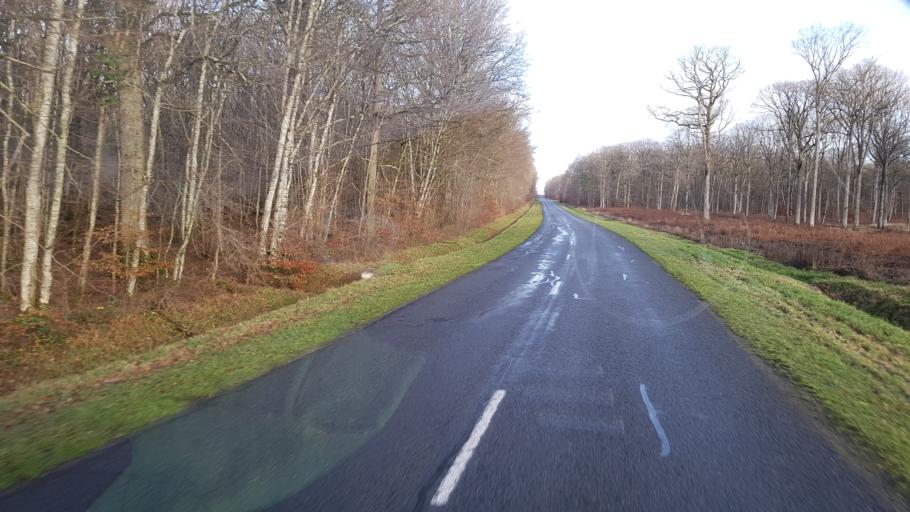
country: FR
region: Centre
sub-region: Departement du Loiret
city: Chilleurs-aux-Bois
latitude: 48.0269
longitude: 2.2100
